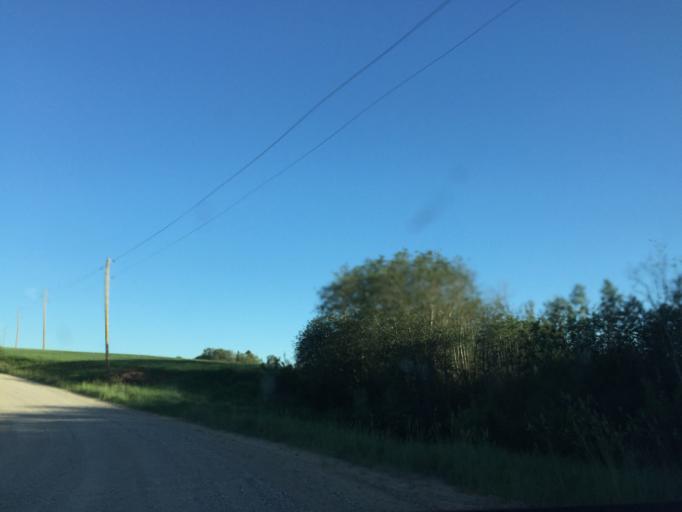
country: LV
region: Broceni
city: Broceni
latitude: 56.7908
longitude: 22.5540
